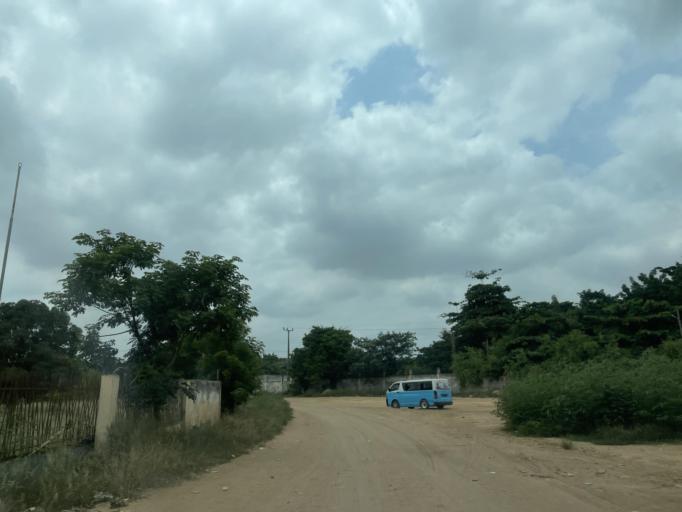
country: AO
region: Luanda
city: Luanda
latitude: -8.9115
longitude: 13.3781
